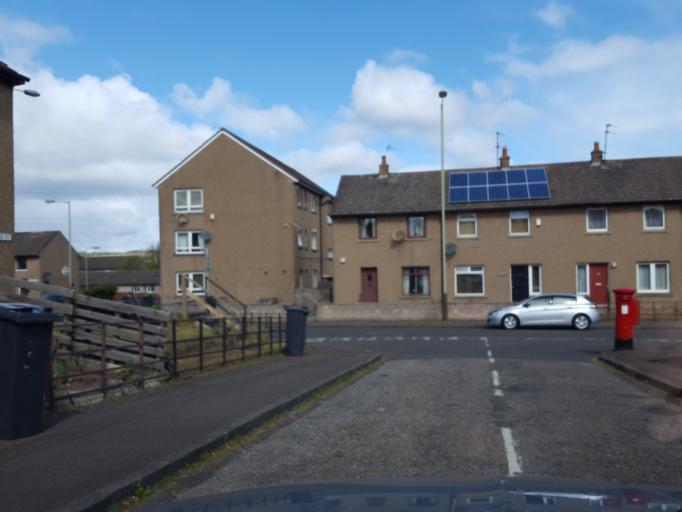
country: GB
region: Scotland
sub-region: Angus
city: Muirhead
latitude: 56.4722
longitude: -3.0470
